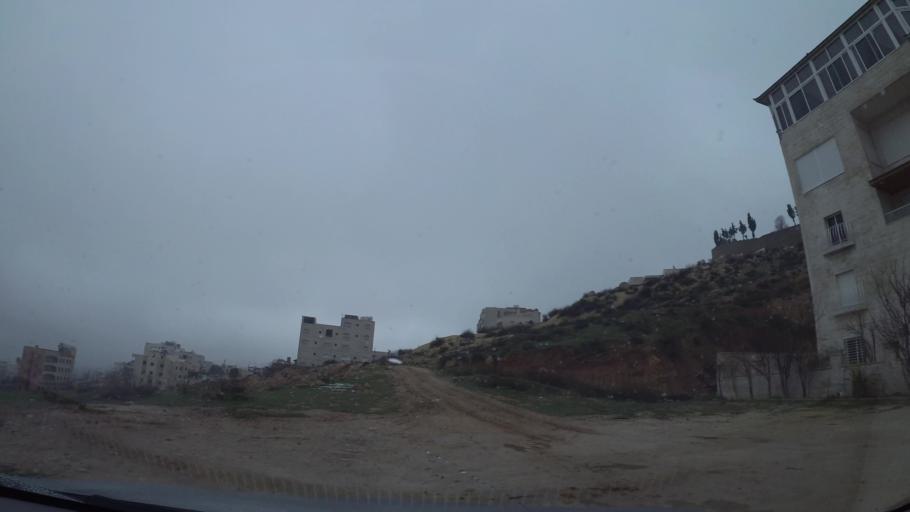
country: JO
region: Amman
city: Al Jubayhah
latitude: 32.0365
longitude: 35.8559
